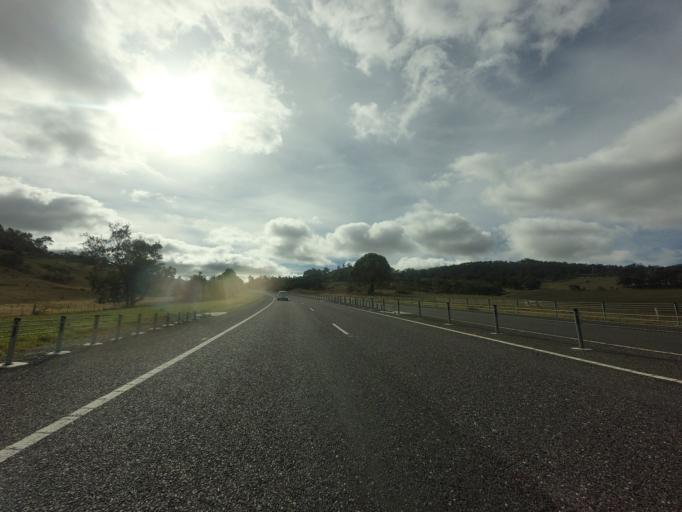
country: AU
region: Tasmania
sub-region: Brighton
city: Bridgewater
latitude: -42.4373
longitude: 147.2592
